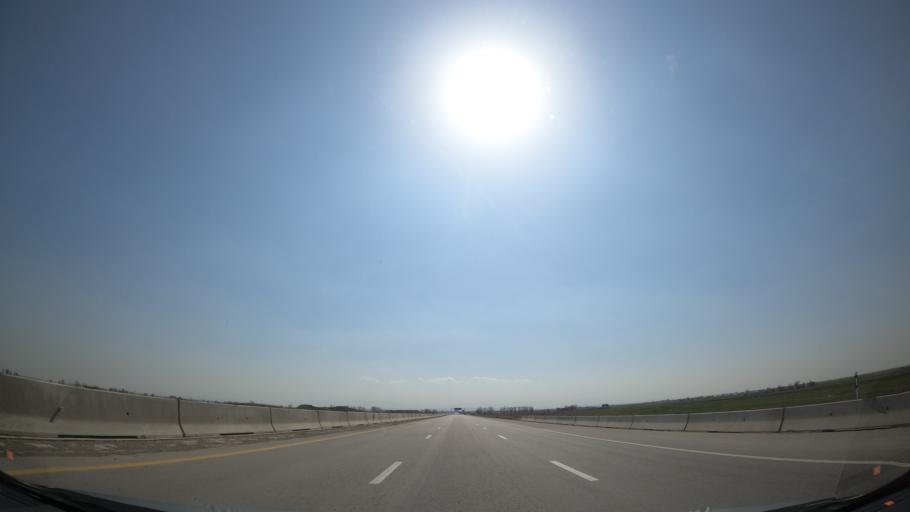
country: IR
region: Qazvin
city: Abyek
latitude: 35.9854
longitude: 50.4620
